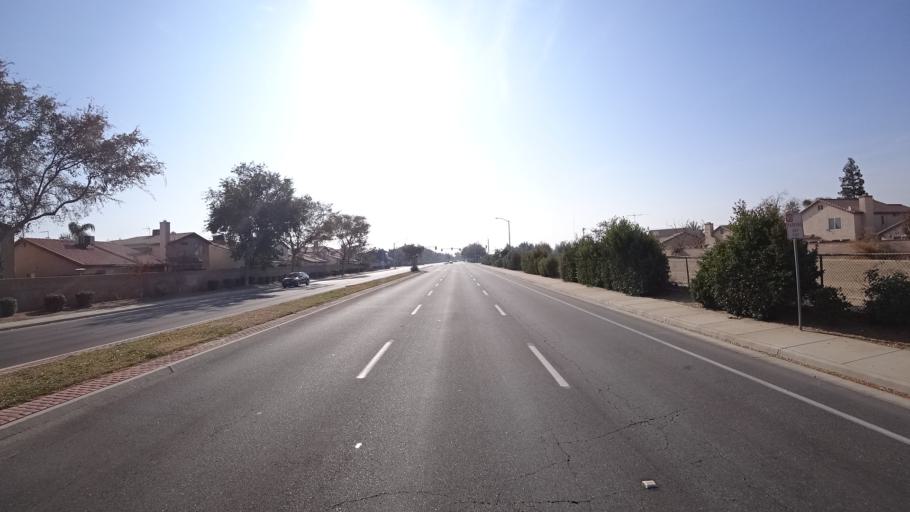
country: US
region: California
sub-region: Kern County
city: Greenacres
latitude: 35.3190
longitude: -119.1095
